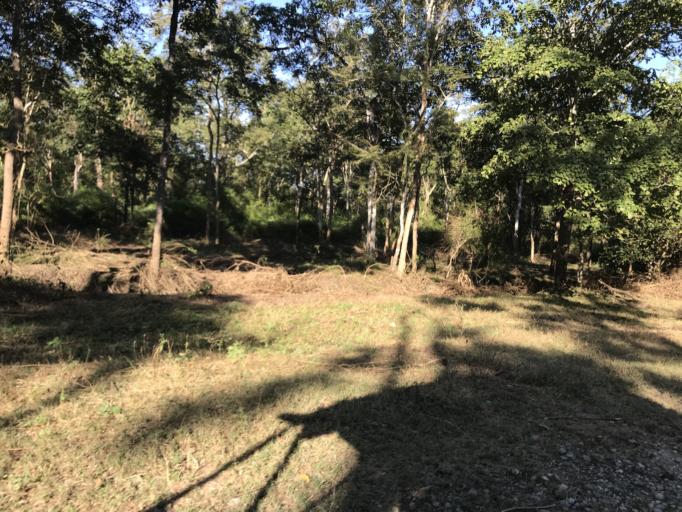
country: IN
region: Karnataka
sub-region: Mysore
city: Heggadadevankote
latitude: 11.9788
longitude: 76.2362
